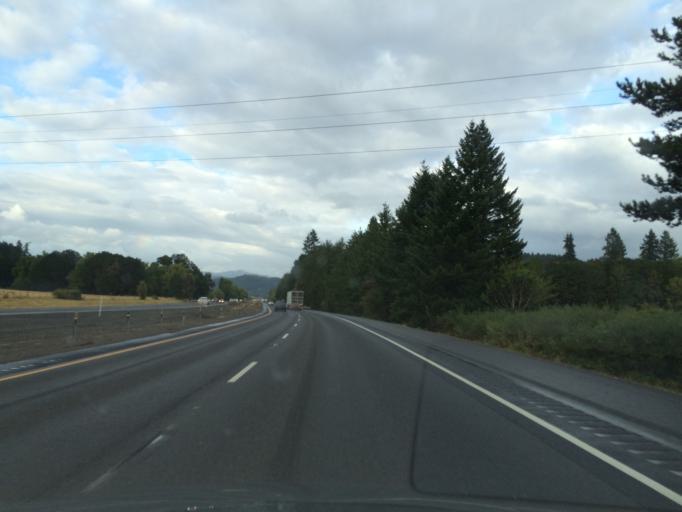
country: US
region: Oregon
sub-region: Lane County
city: Cottage Grove
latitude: 43.7506
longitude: -123.1112
